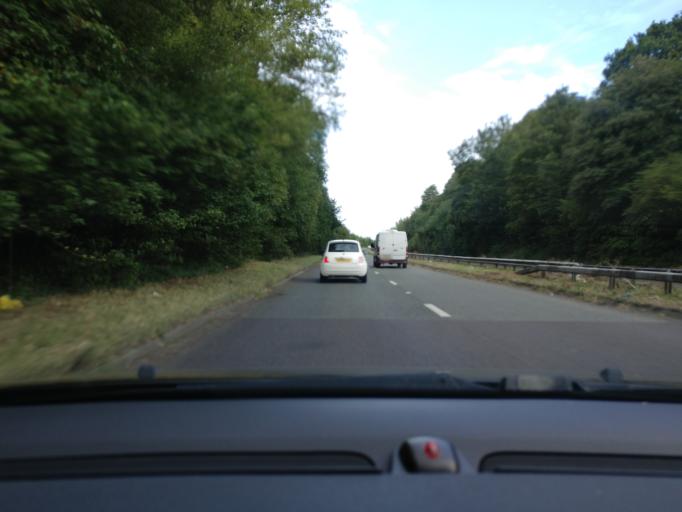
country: GB
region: England
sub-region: Oxfordshire
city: Cowley
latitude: 51.7164
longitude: -1.2292
